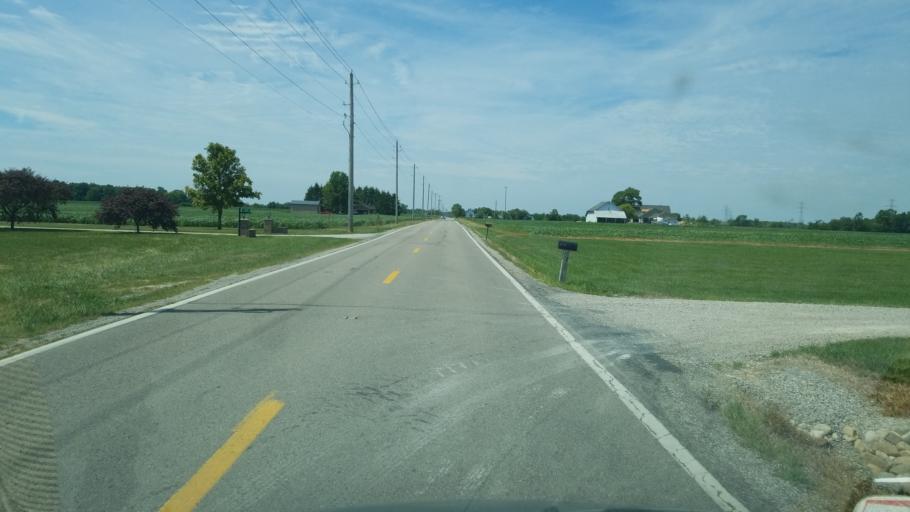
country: US
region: Ohio
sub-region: Franklin County
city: Grove City
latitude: 39.8603
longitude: -83.1332
